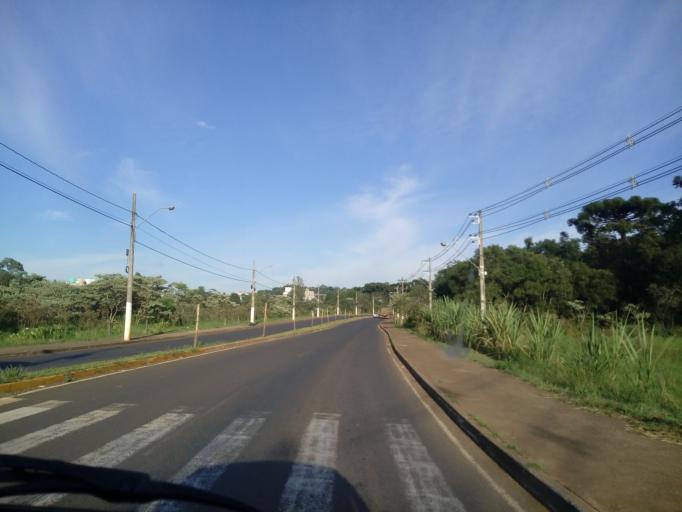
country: BR
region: Santa Catarina
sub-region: Chapeco
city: Chapeco
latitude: -27.0893
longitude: -52.6671
